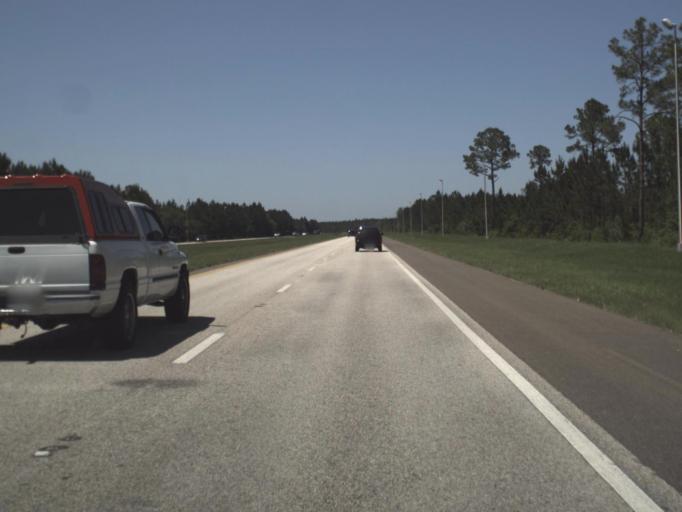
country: US
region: Florida
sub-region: Clay County
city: Bellair-Meadowbrook Terrace
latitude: 30.2052
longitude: -81.8372
